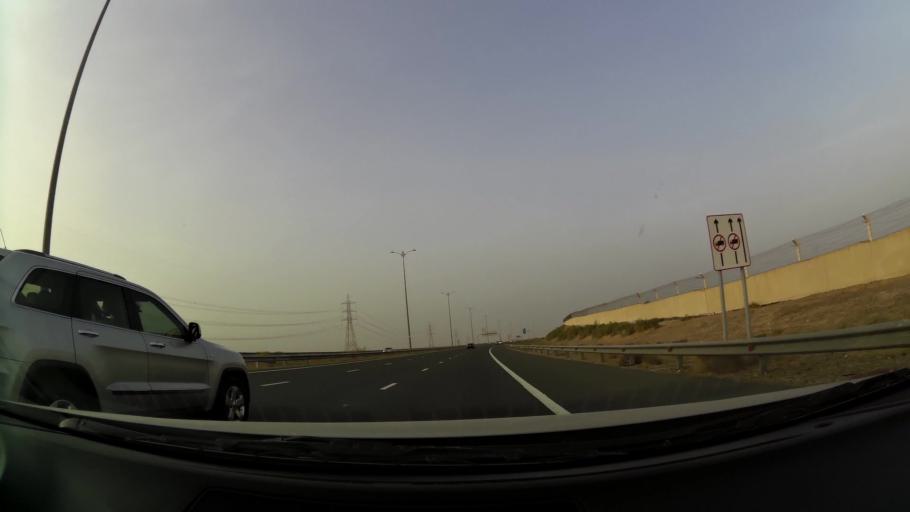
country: OM
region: Al Buraimi
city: Al Buraymi
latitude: 24.3304
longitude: 55.7614
